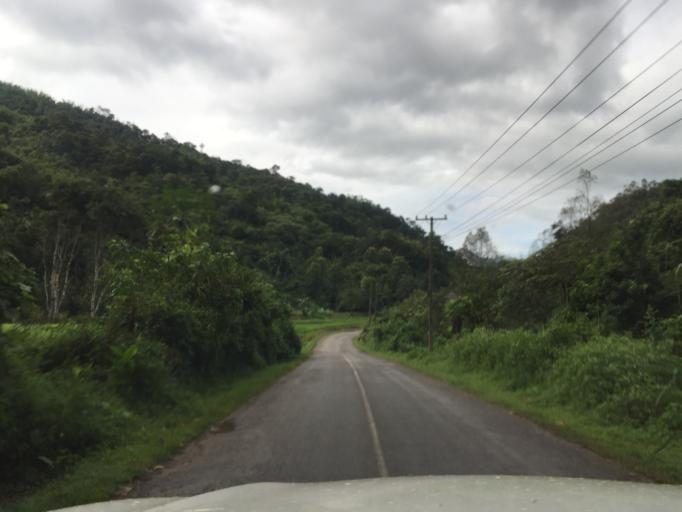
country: LA
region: Oudomxai
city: Muang La
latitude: 20.8071
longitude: 102.0882
